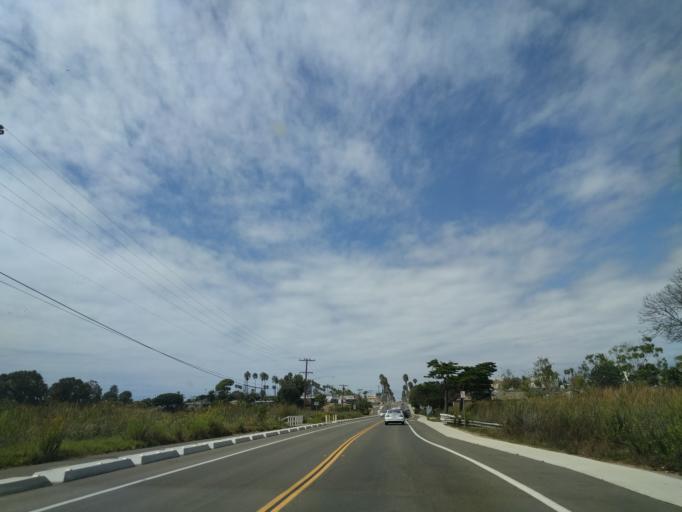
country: US
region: California
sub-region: San Diego County
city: Carlsbad
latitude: 33.1677
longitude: -117.3558
